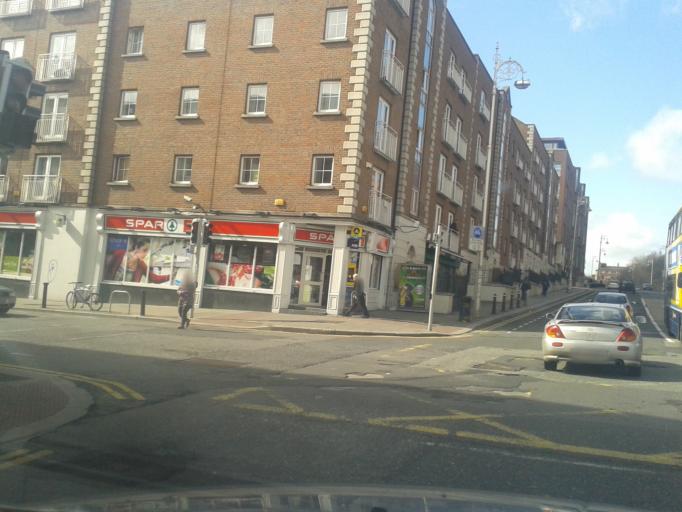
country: IE
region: Leinster
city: Drumcondra
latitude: 53.3541
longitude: -6.2569
